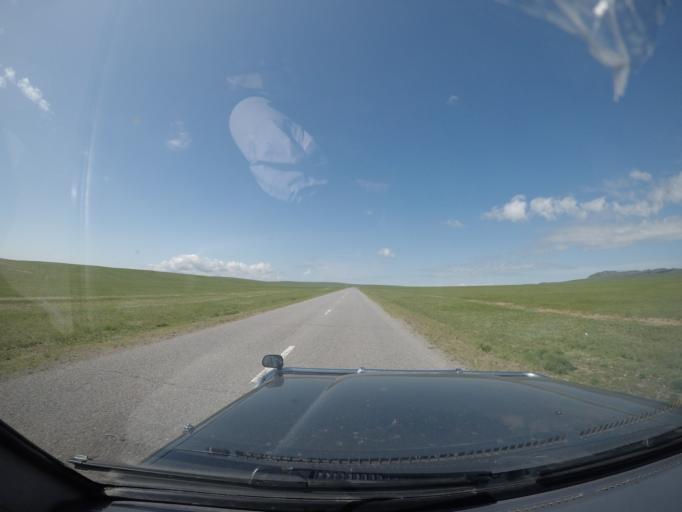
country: MN
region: Hentiy
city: Bayan
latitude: 47.3169
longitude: 111.3690
